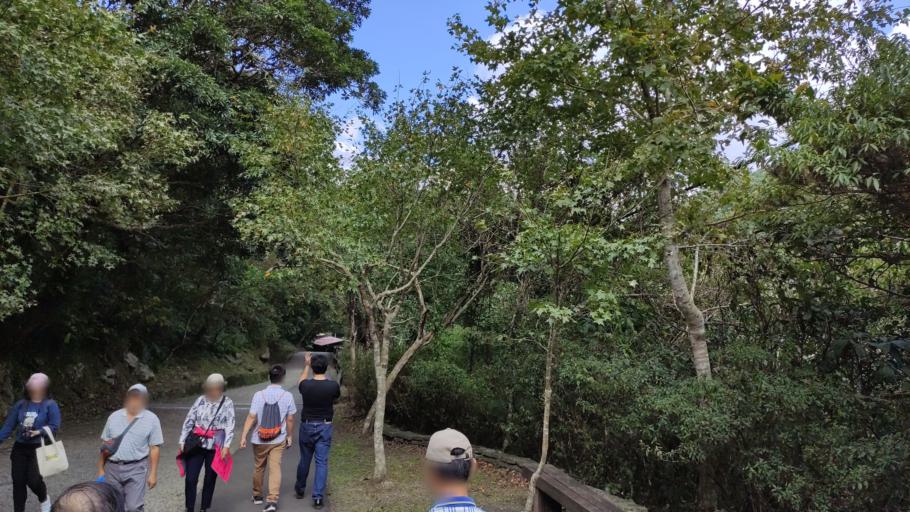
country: TW
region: Taiwan
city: Daxi
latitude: 24.8295
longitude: 121.4445
